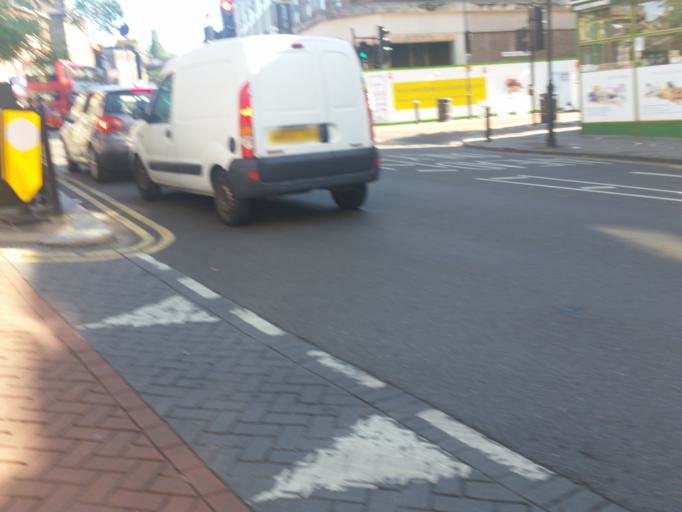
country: GB
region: England
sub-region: Greater London
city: Crouch End
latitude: 51.5799
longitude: -0.1238
